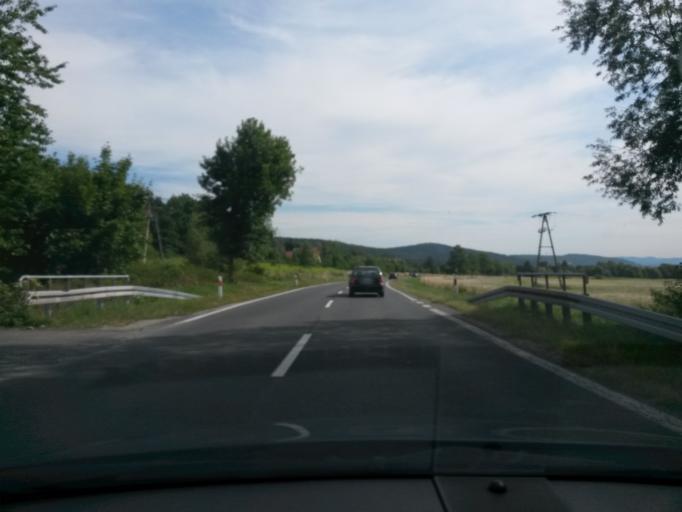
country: PL
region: Lower Silesian Voivodeship
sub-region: Powiat jeleniogorski
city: Piechowice
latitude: 50.8756
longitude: 15.6236
